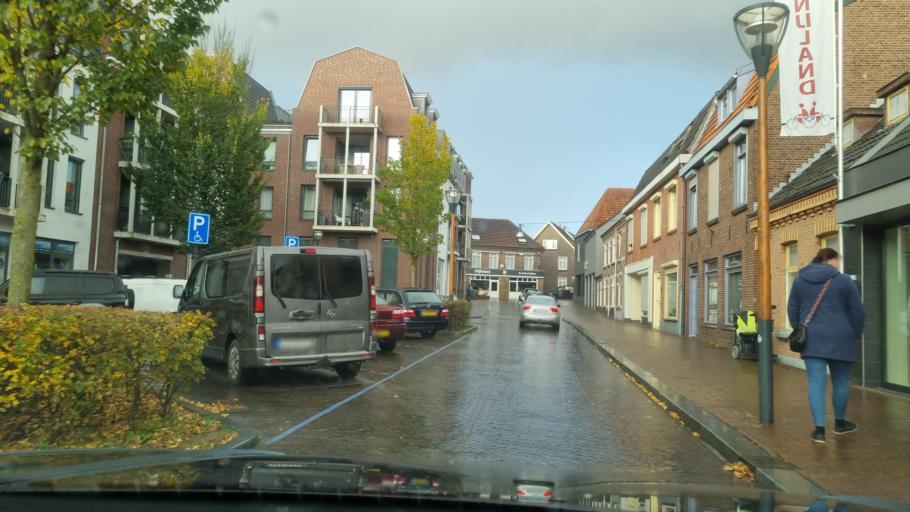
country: NL
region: Gelderland
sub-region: Gemeente Montferland
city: s-Heerenberg
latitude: 51.8753
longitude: 6.2462
